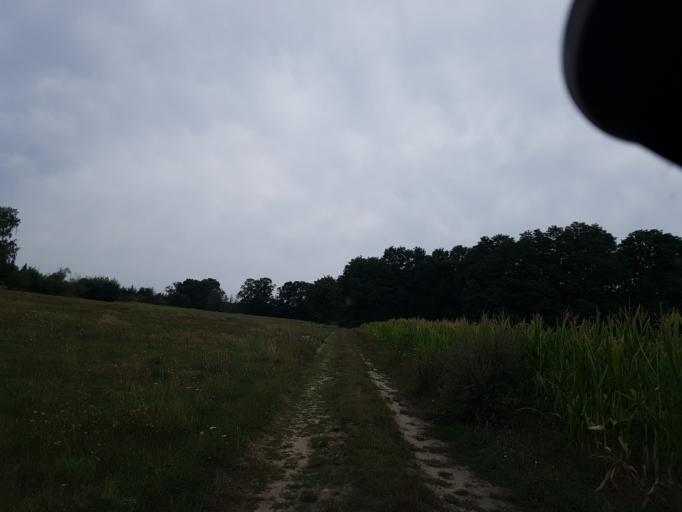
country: DE
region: Brandenburg
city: Finsterwalde
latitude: 51.6132
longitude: 13.6494
